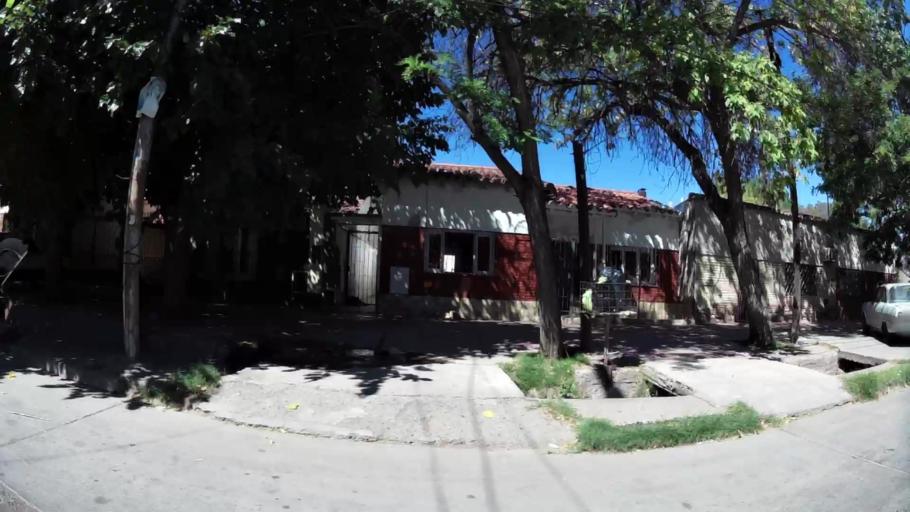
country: AR
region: Mendoza
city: Las Heras
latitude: -32.8447
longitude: -68.8339
